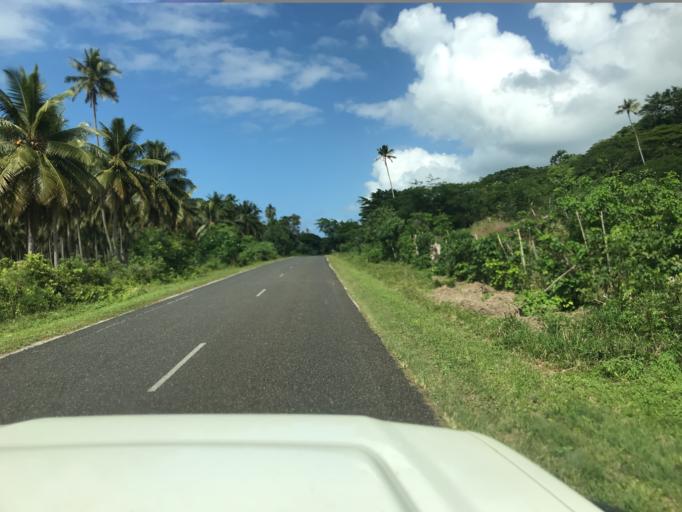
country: VU
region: Sanma
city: Luganville
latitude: -15.3998
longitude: 167.1990
